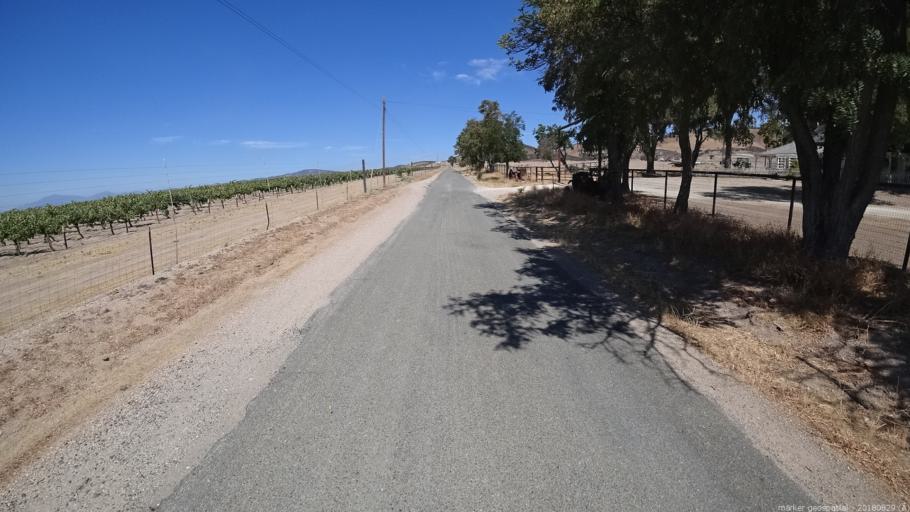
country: US
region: California
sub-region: San Luis Obispo County
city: Lake Nacimiento
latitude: 35.9159
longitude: -121.0379
